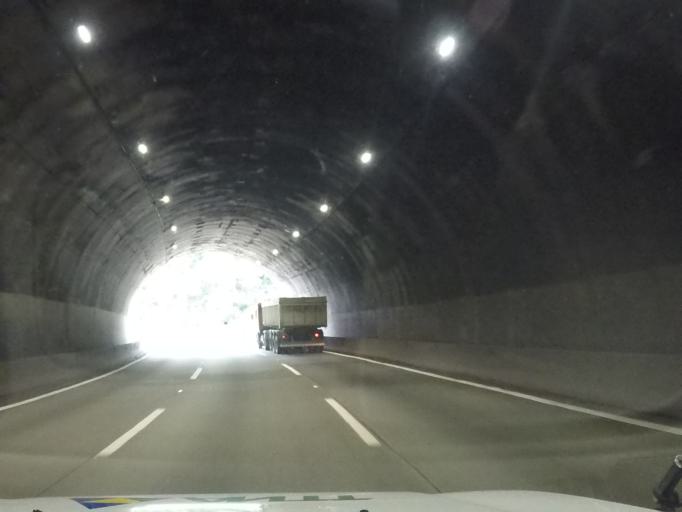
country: BR
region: Sao Paulo
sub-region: Mairipora
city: Mairipora
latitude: -23.3560
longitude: -46.5484
